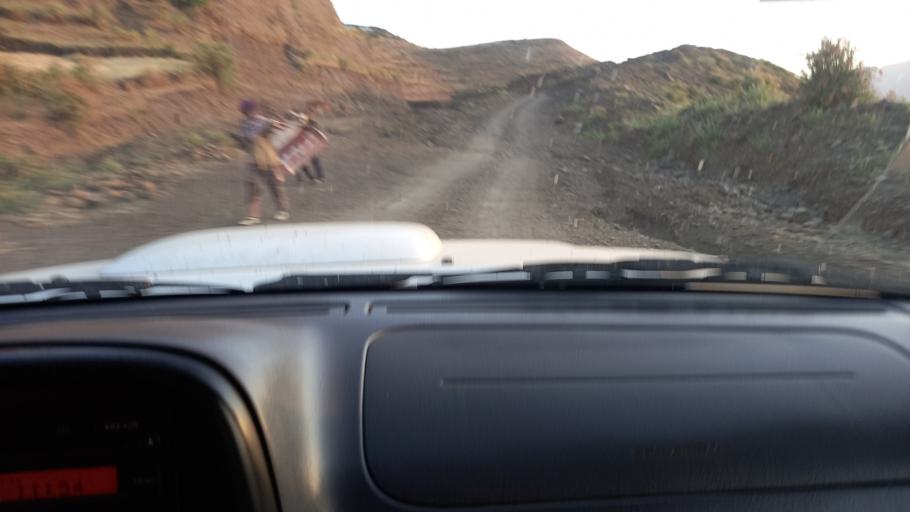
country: ET
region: Amhara
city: Debark'
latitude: 13.0517
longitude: 38.0198
